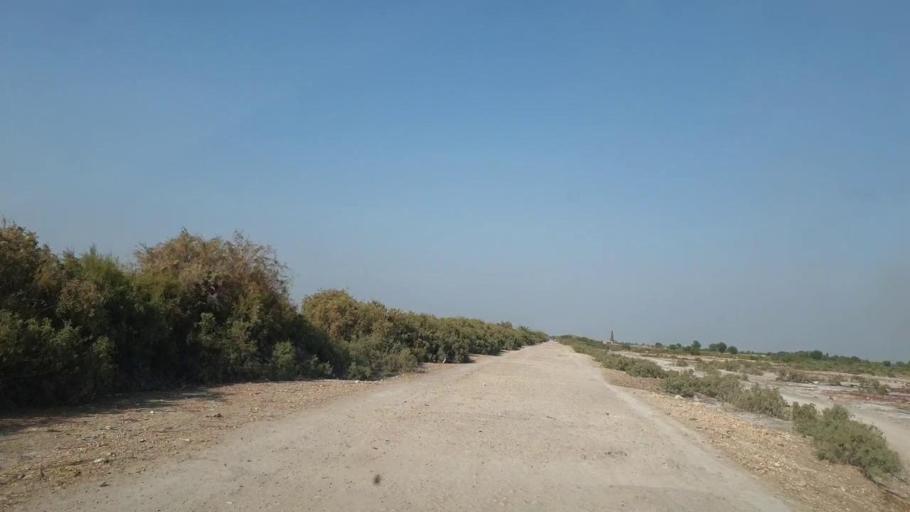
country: PK
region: Sindh
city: Tando Mittha Khan
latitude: 25.7336
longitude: 69.1898
